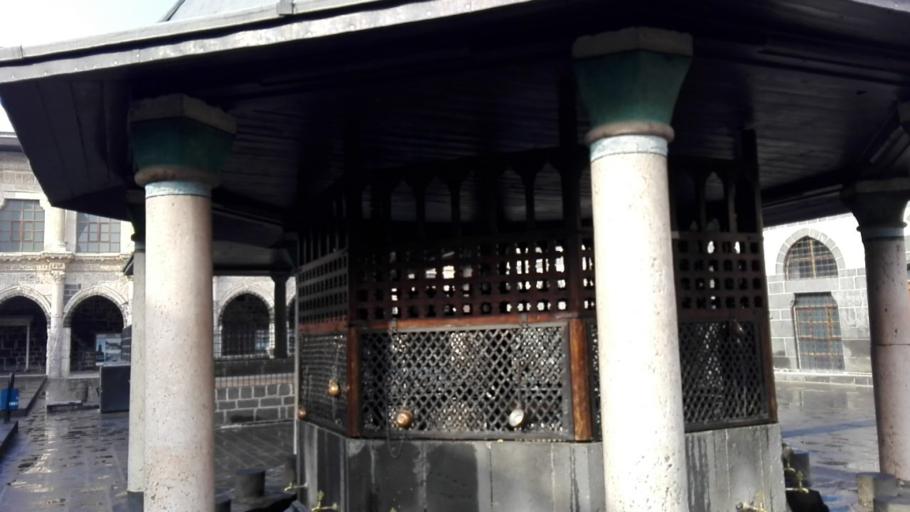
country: TR
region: Diyarbakir
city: Sur
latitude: 37.9124
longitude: 40.2359
